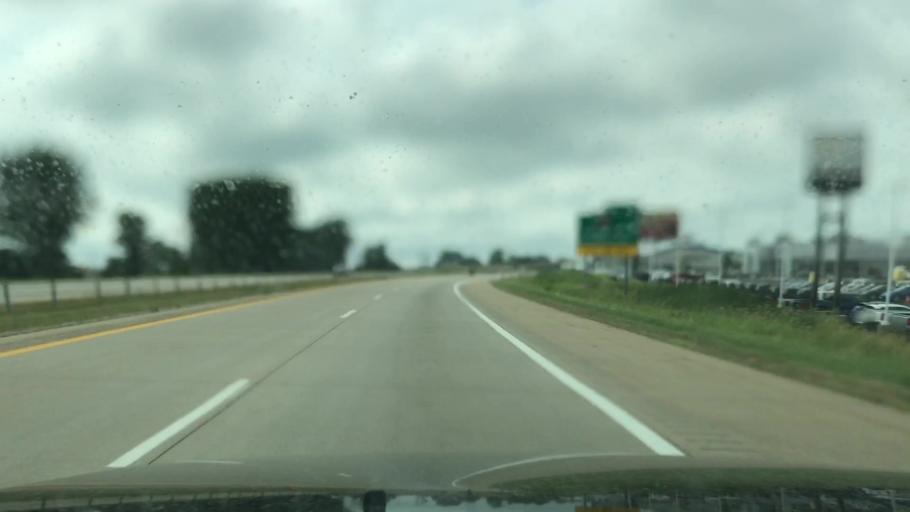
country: US
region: Michigan
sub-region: Ottawa County
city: Coopersville
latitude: 43.0534
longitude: -85.9502
